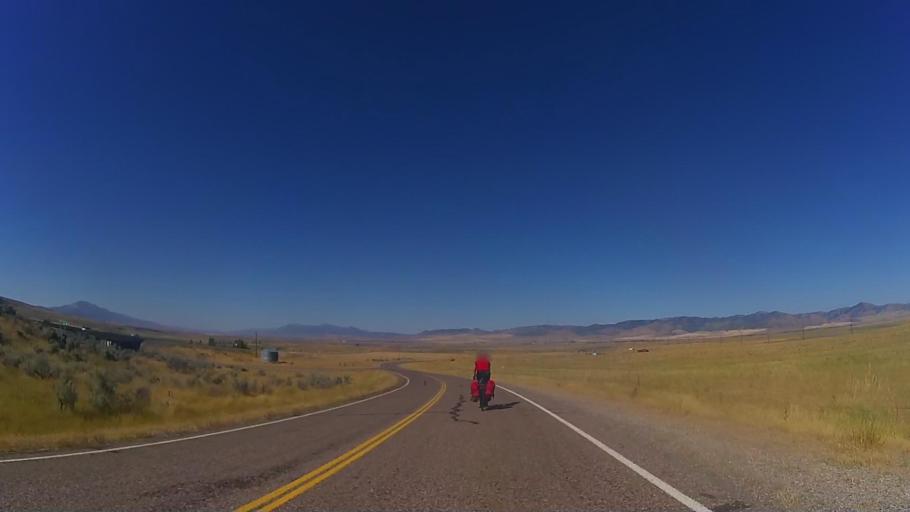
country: US
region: Idaho
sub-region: Oneida County
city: Malad City
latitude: 42.3726
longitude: -112.2098
